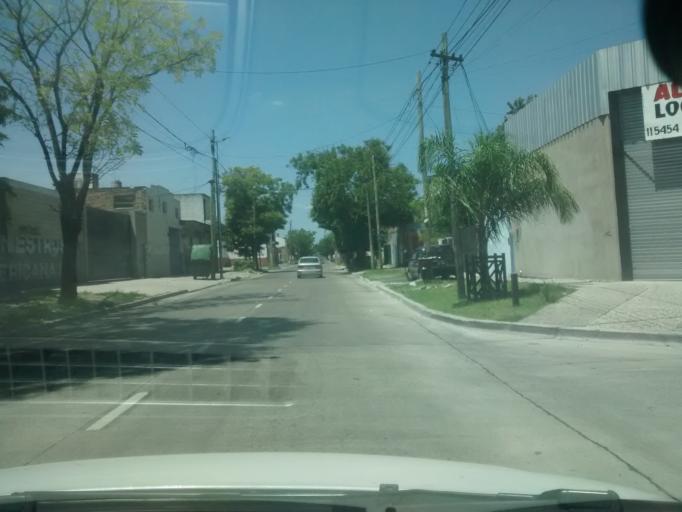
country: AR
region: Buenos Aires
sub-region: Partido de Moron
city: Moron
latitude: -34.6611
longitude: -58.6066
